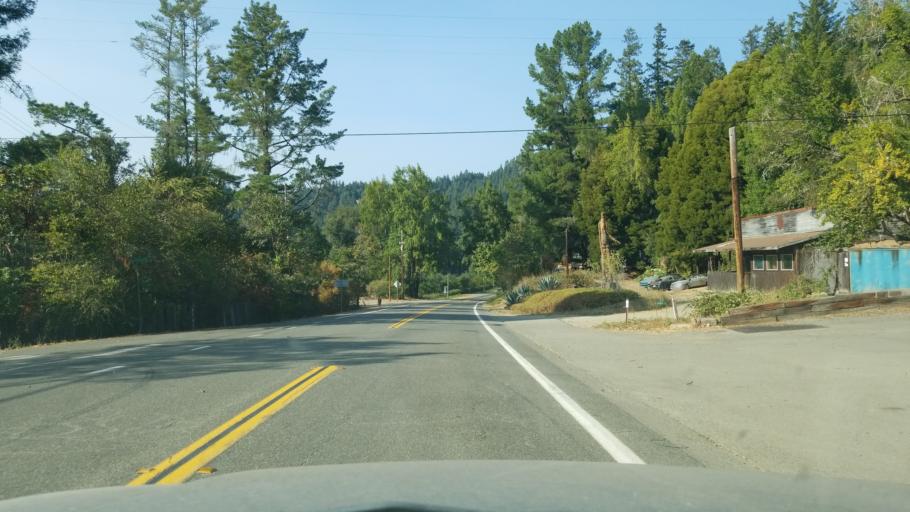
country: US
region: California
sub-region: Humboldt County
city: Redway
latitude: 40.2114
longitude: -123.7867
